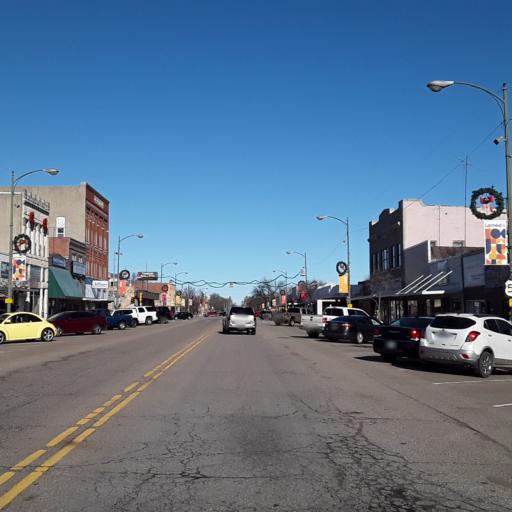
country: US
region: Kansas
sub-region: Pawnee County
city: Larned
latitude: 38.1788
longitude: -99.0983
